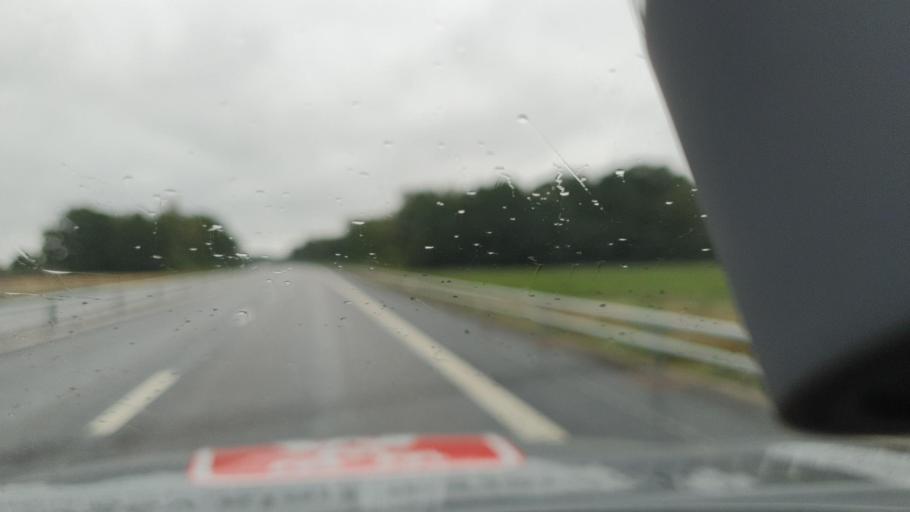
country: SE
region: Skane
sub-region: Kristianstads Kommun
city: Onnestad
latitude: 55.9612
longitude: 13.9904
